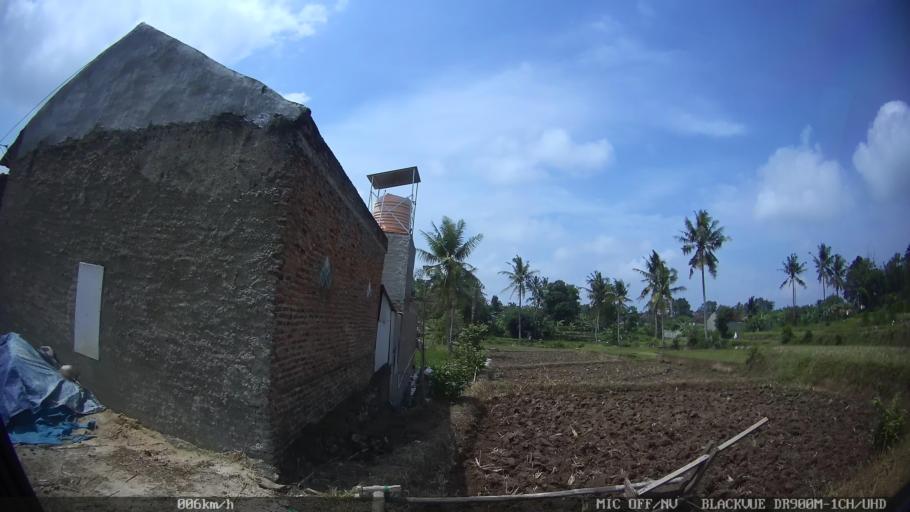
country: ID
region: Lampung
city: Kedaton
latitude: -5.3314
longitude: 105.2961
